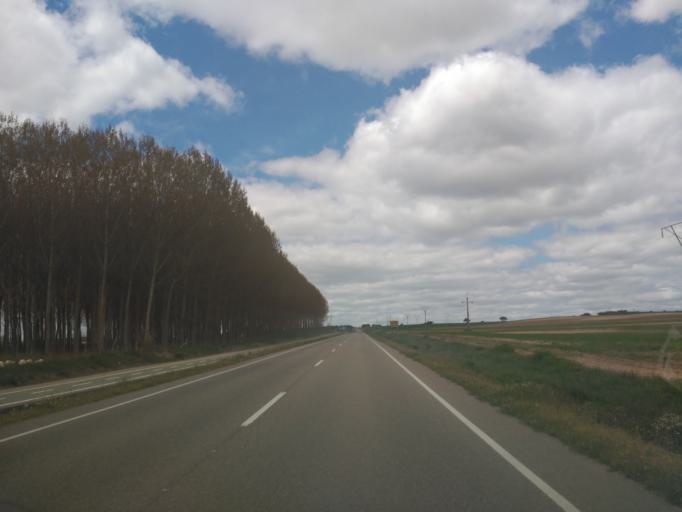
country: ES
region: Castille and Leon
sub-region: Provincia de Salamanca
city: Villamayor
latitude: 41.0245
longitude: -5.7233
